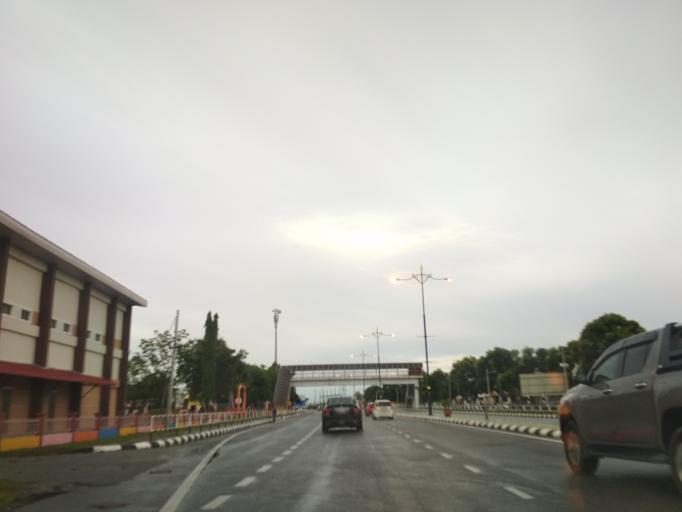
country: MY
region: Perlis
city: Kangar
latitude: 6.4369
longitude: 100.2062
